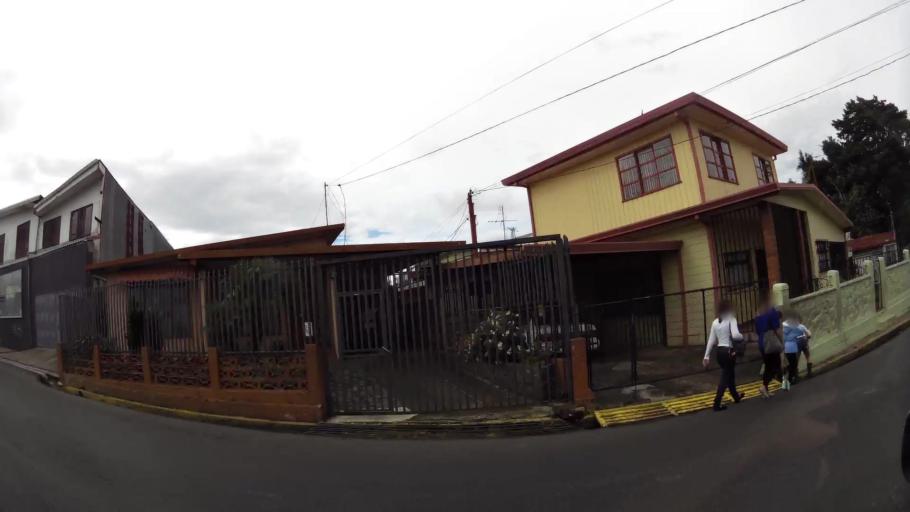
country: CR
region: San Jose
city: San Vicente de Moravia
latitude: 9.9630
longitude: -84.0531
